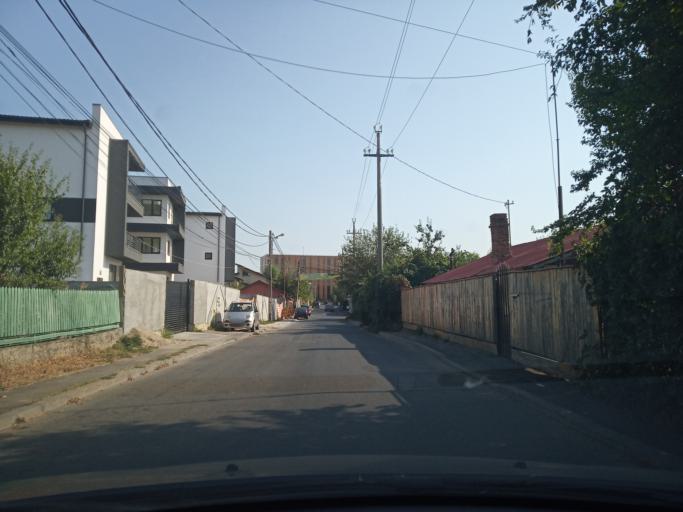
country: RO
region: Ilfov
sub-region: Comuna Corbeanca
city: Corbeanca
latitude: 44.6055
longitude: 26.0744
